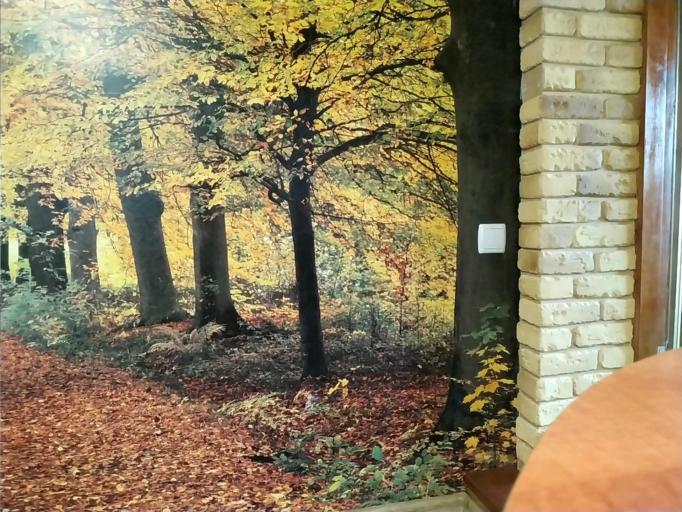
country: RU
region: Leningrad
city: Tolmachevo
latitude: 58.9333
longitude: 29.7056
